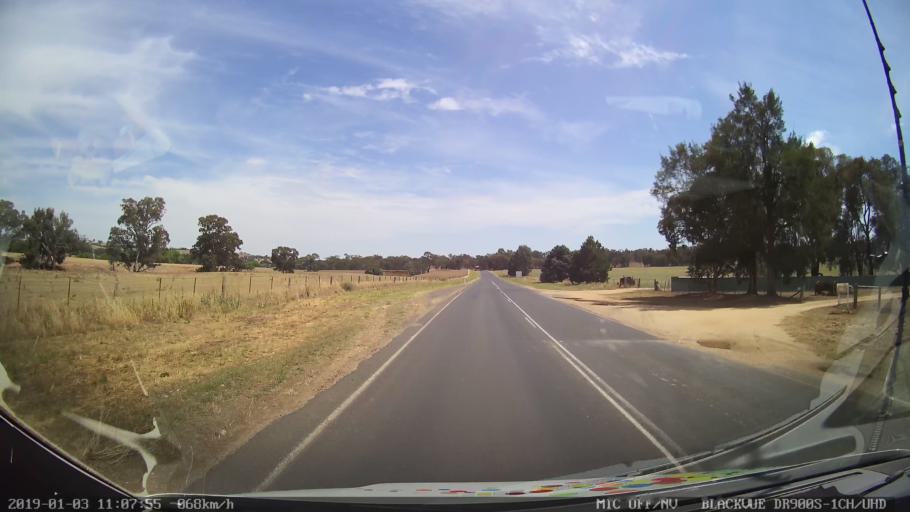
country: AU
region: New South Wales
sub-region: Young
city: Young
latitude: -34.2547
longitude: 148.2589
